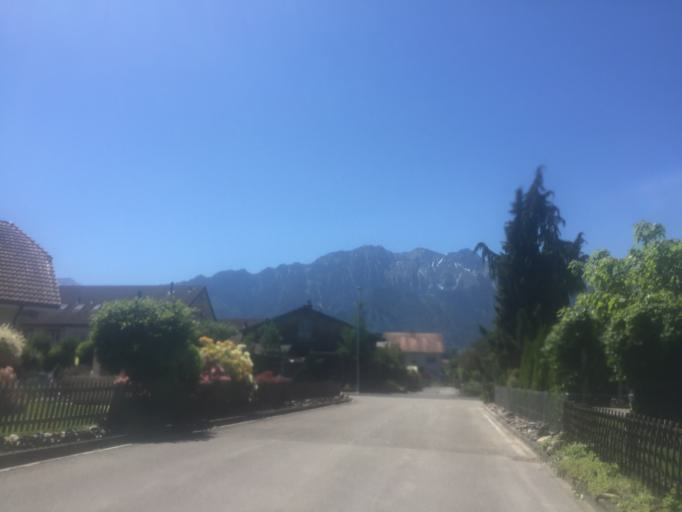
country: CH
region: Bern
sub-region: Thun District
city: Thierachern
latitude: 46.7449
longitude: 7.5934
